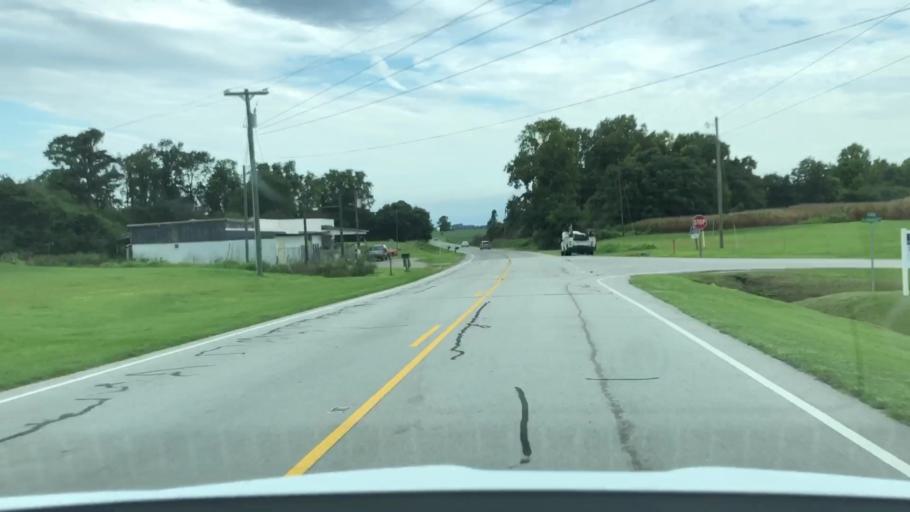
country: US
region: North Carolina
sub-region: Lenoir County
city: Kinston
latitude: 35.1379
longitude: -77.5292
